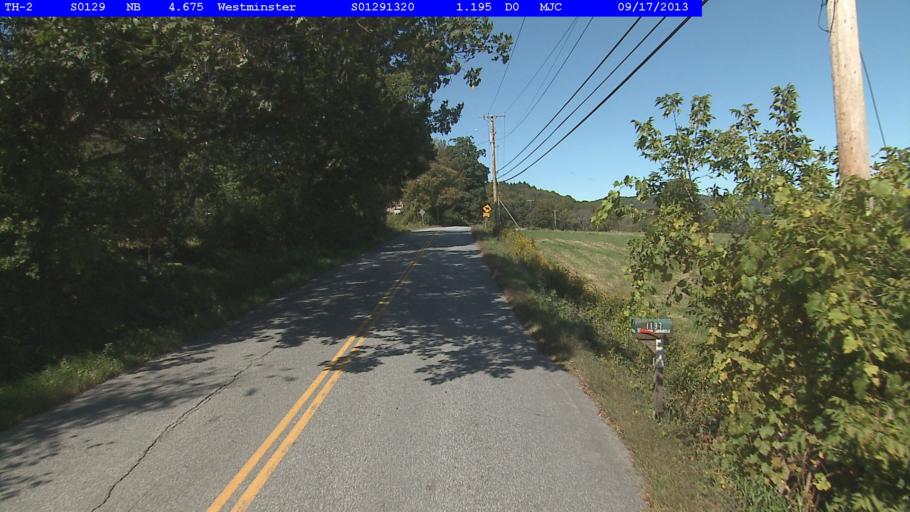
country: US
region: New Hampshire
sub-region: Cheshire County
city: Westmoreland
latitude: 43.0380
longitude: -72.5259
